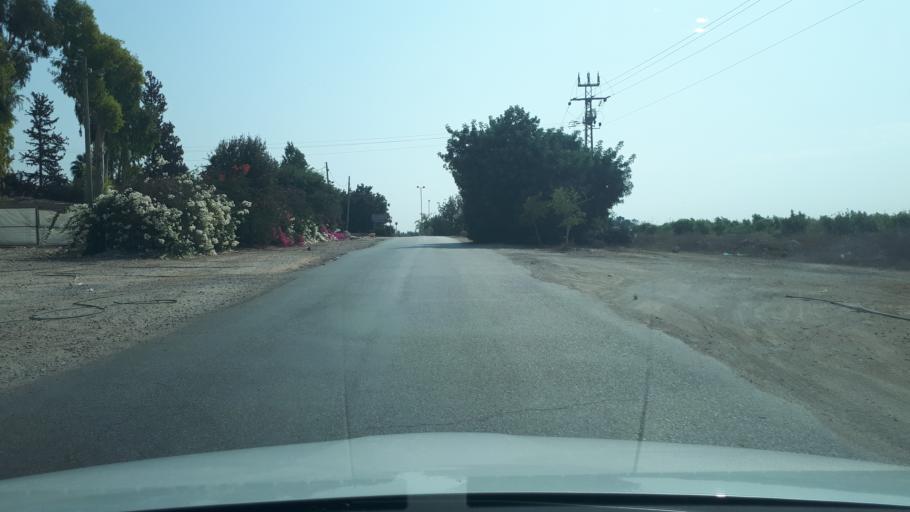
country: IL
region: Central District
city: Rosh Ha'Ayin
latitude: 32.0633
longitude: 34.9462
